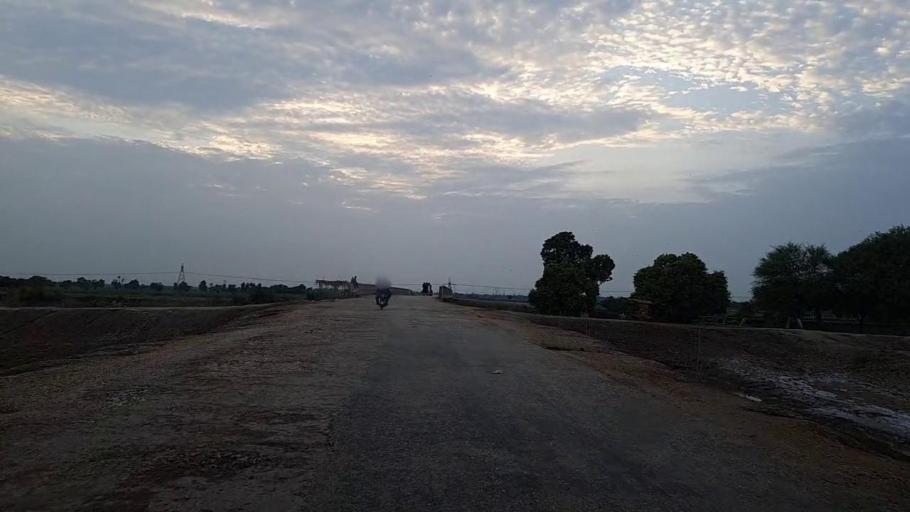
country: PK
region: Sindh
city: Naushahro Firoz
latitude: 26.8236
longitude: 68.1600
